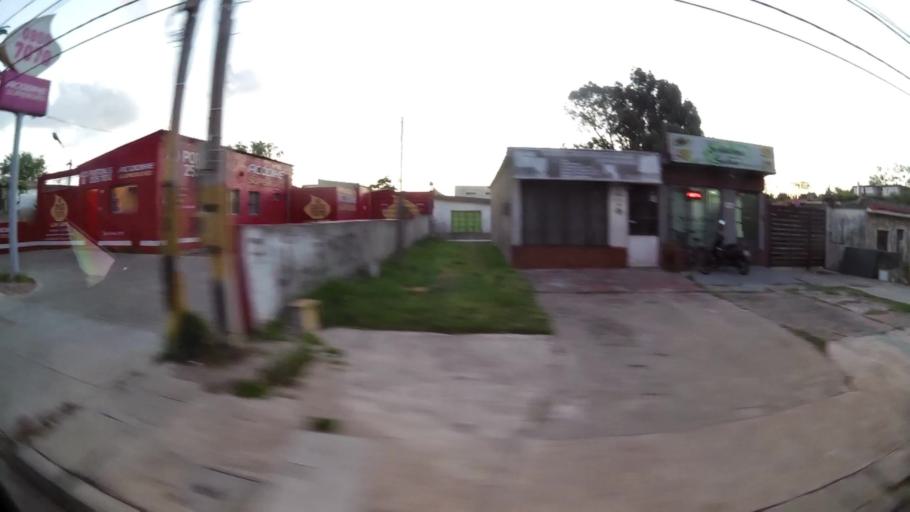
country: UY
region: Canelones
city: Paso de Carrasco
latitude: -34.8776
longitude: -56.1015
